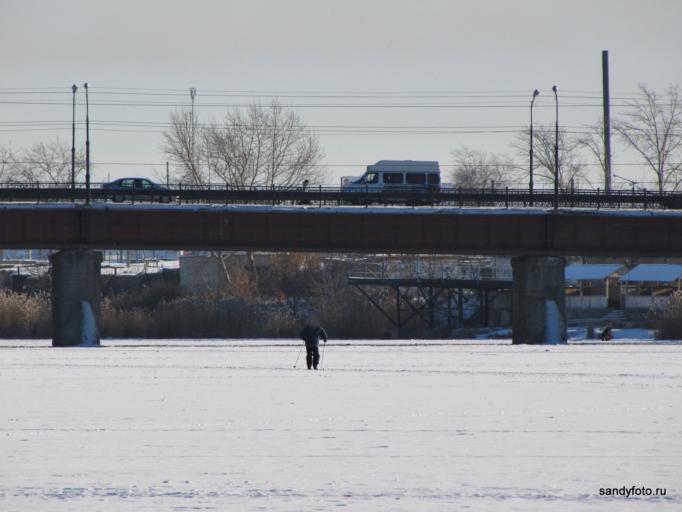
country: RU
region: Chelyabinsk
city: Troitsk
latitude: 54.0946
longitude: 61.5601
